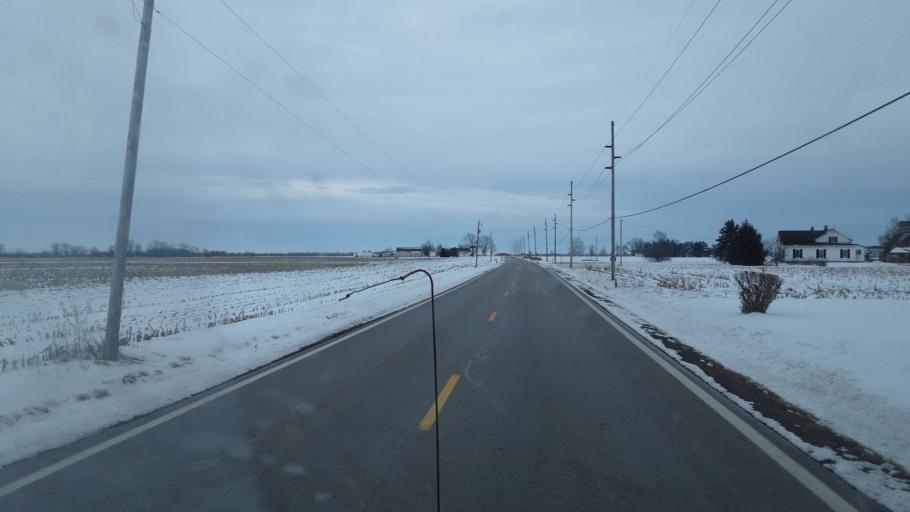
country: US
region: Ohio
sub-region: Madison County
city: Mount Sterling
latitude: 39.6932
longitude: -83.2231
